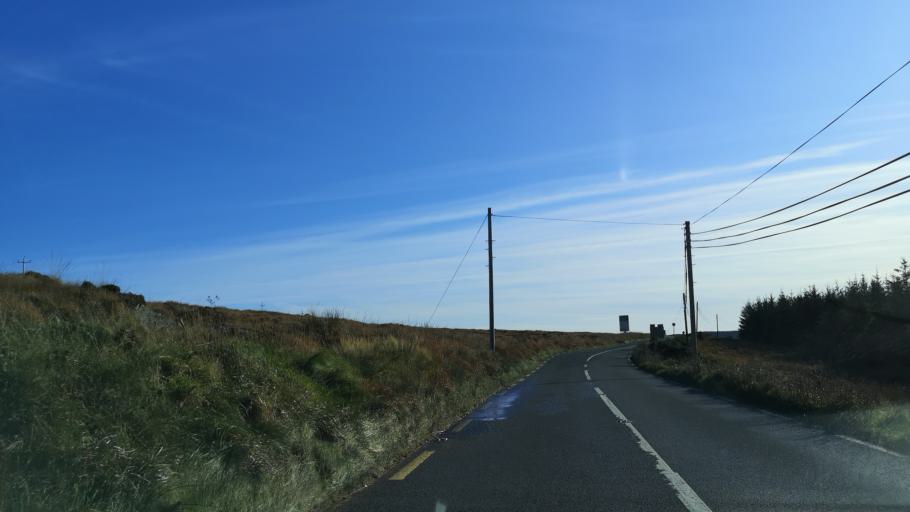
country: IE
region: Connaught
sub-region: County Galway
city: Clifden
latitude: 53.5258
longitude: -10.0478
